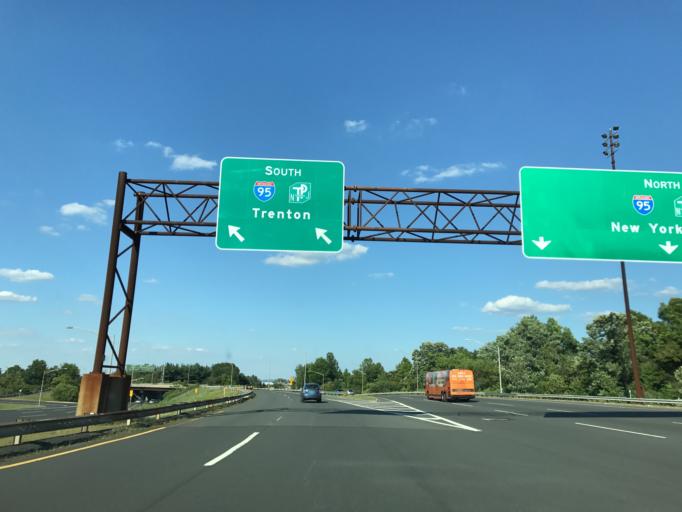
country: US
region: New Jersey
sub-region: Middlesex County
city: Woodbridge
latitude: 40.5402
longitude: -74.2972
